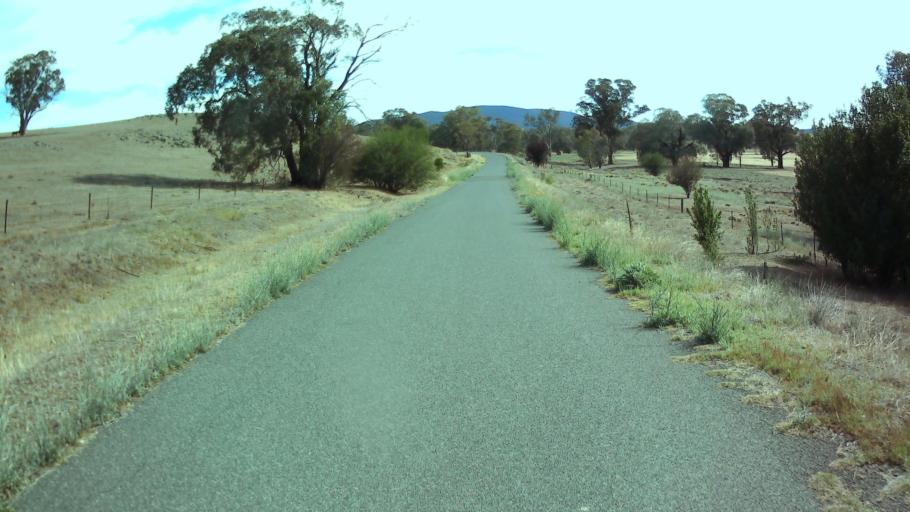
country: AU
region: New South Wales
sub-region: Weddin
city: Grenfell
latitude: -33.8196
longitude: 148.2904
